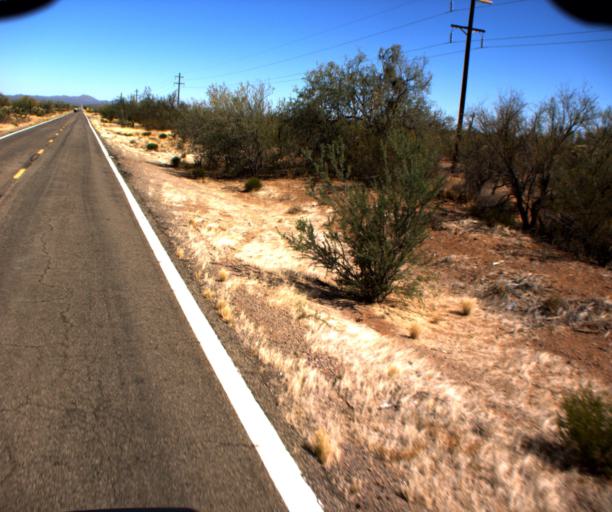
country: US
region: Arizona
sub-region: Pima County
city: Sells
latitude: 32.0308
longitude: -112.0099
